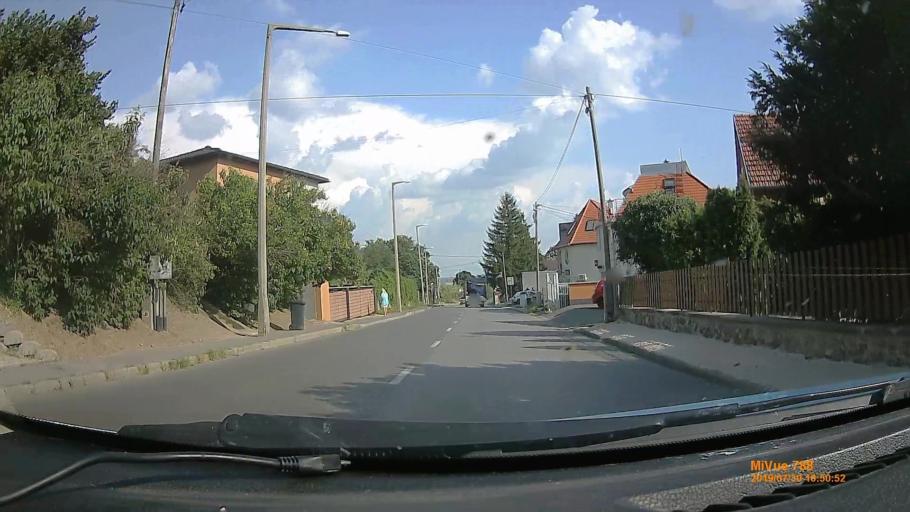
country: HU
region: Baranya
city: Pecs
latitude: 46.0809
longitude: 18.2097
